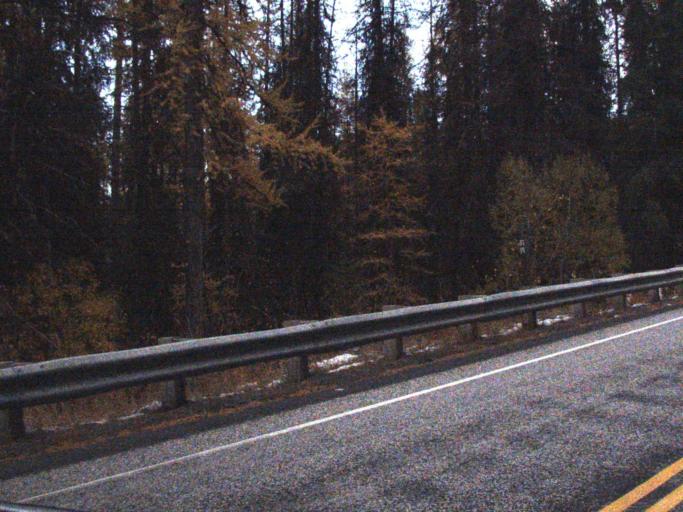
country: US
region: Washington
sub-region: Ferry County
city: Republic
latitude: 48.6217
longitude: -118.4444
